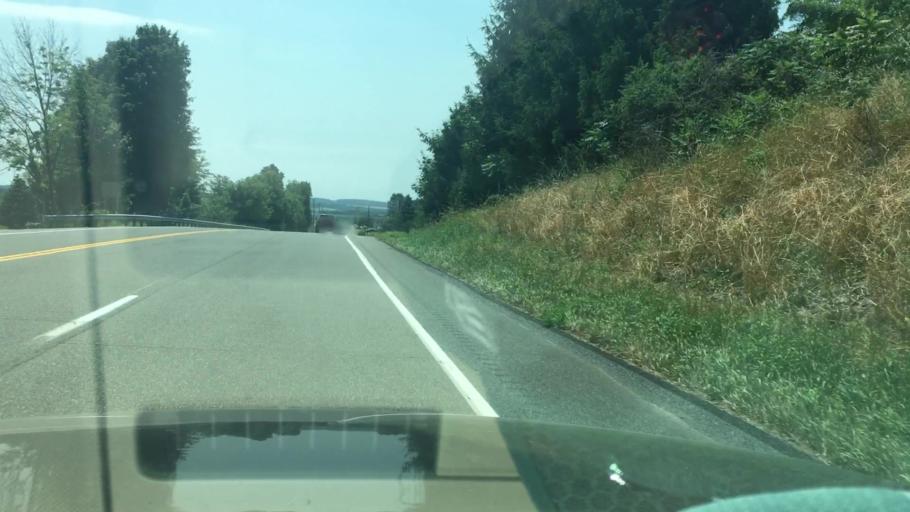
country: US
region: Pennsylvania
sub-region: Lehigh County
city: Schnecksville
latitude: 40.6493
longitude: -75.6839
